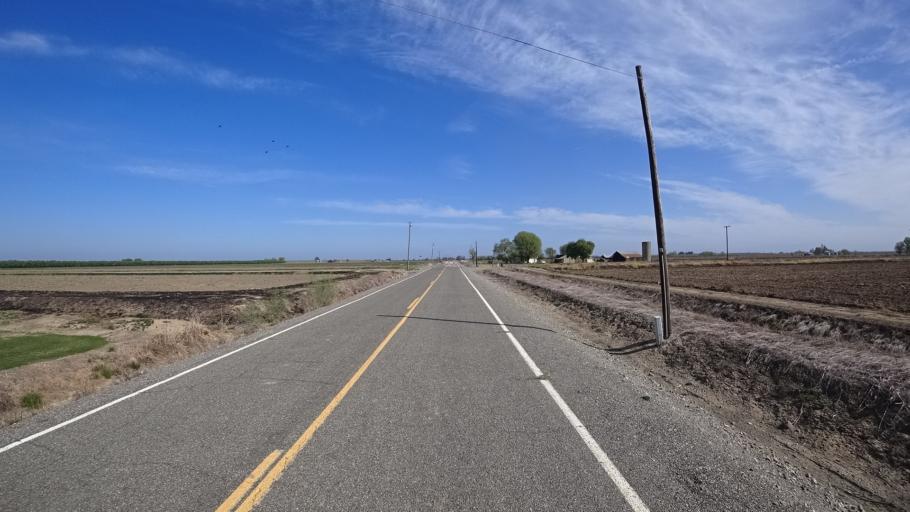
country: US
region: California
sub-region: Glenn County
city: Hamilton City
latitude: 39.6080
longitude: -122.0369
